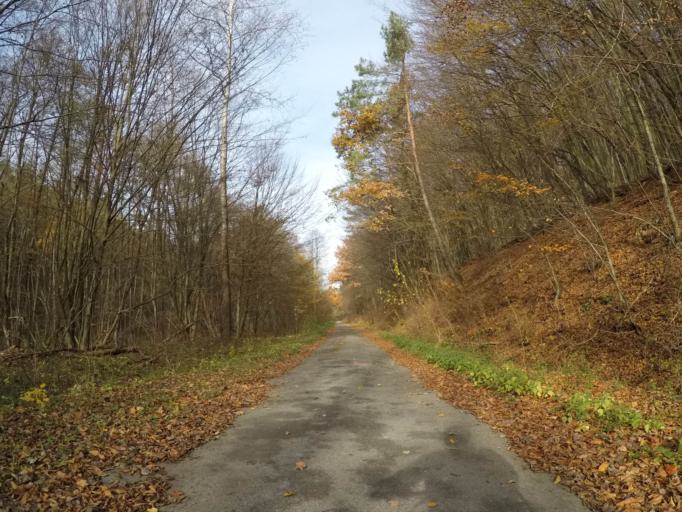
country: SK
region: Presovsky
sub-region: Okres Presov
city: Presov
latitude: 48.9597
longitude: 21.1939
